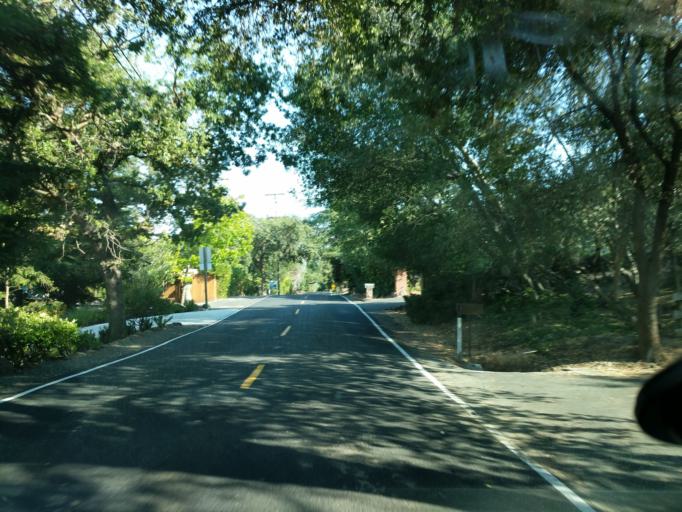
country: US
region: California
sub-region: Contra Costa County
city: Alamo
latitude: 37.8695
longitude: -122.0497
